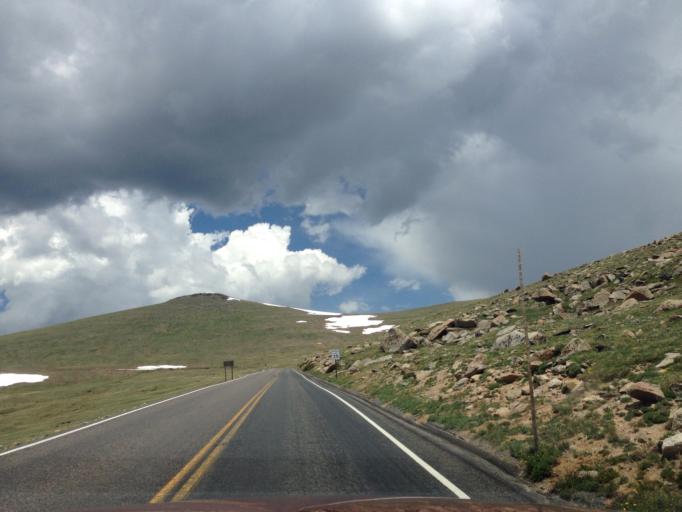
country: US
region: Colorado
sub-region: Larimer County
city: Estes Park
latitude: 40.3967
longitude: -105.7109
